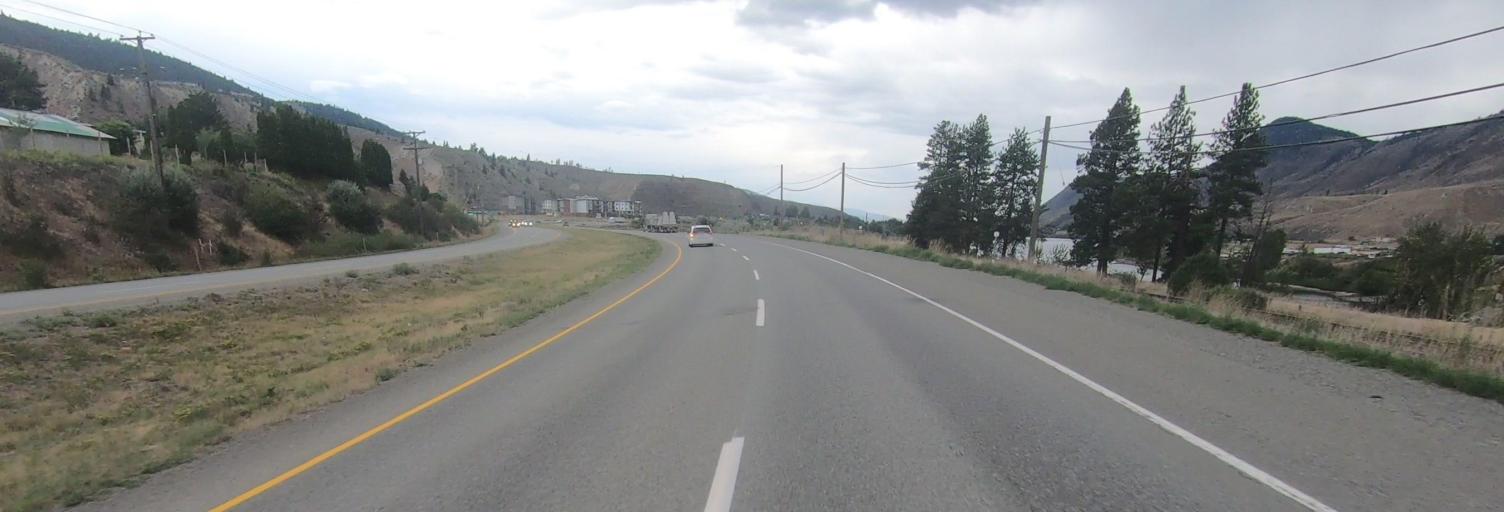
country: CA
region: British Columbia
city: Kamloops
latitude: 50.6718
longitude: -120.2136
